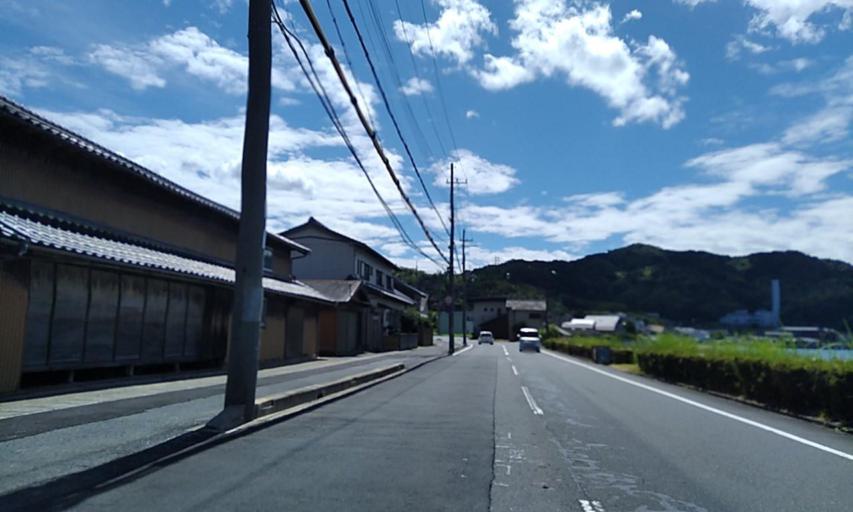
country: JP
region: Kyoto
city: Miyazu
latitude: 35.5543
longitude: 135.2075
